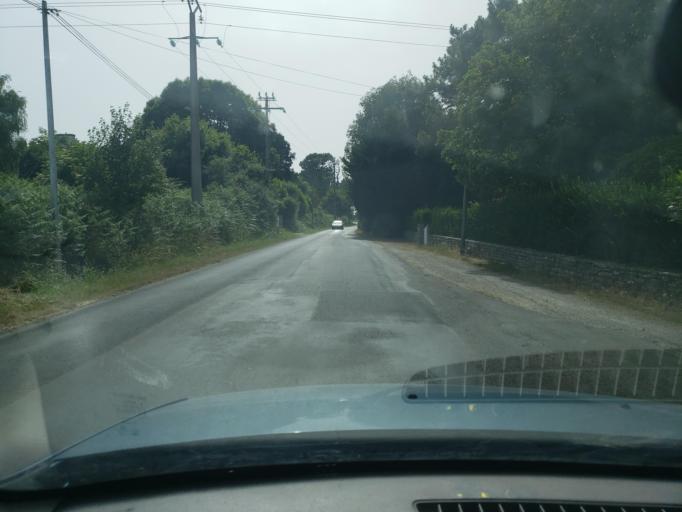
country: FR
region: Brittany
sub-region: Departement du Finistere
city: Plobannalec-Lesconil
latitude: 47.8081
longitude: -4.2267
